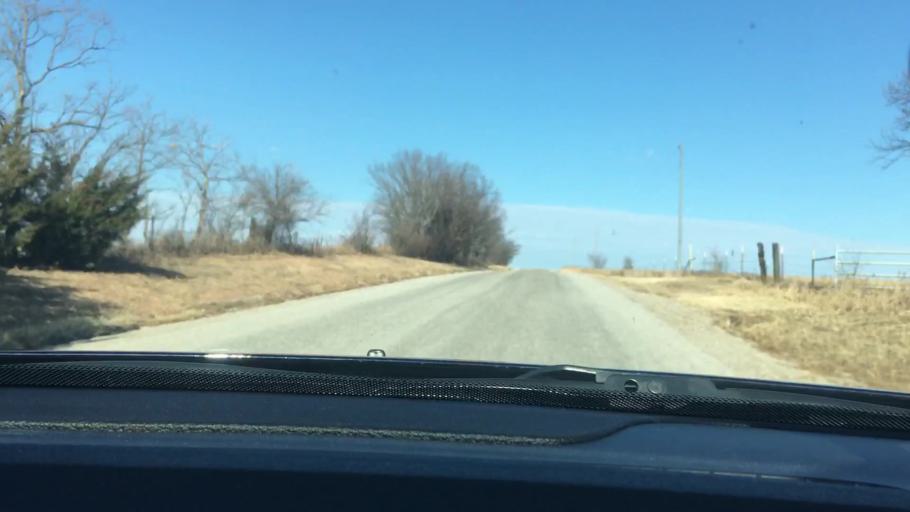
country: US
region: Oklahoma
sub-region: Garvin County
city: Wynnewood
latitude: 34.6547
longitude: -97.0901
